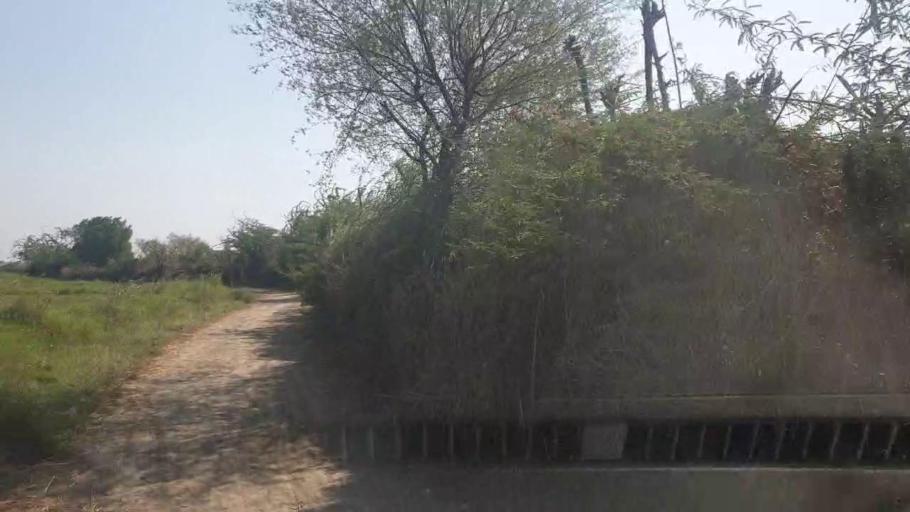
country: PK
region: Sindh
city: Badin
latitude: 24.6812
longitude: 68.8949
